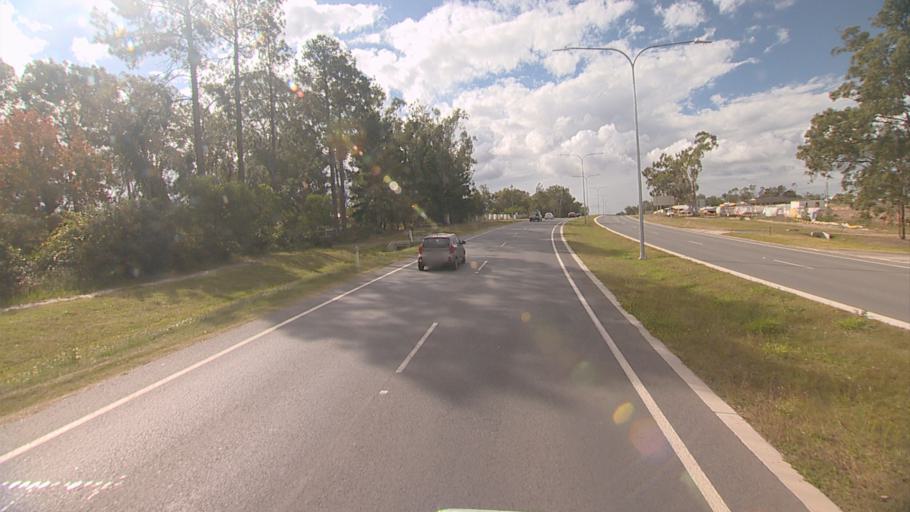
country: AU
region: Queensland
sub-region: Logan
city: Logan Reserve
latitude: -27.7066
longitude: 153.0942
